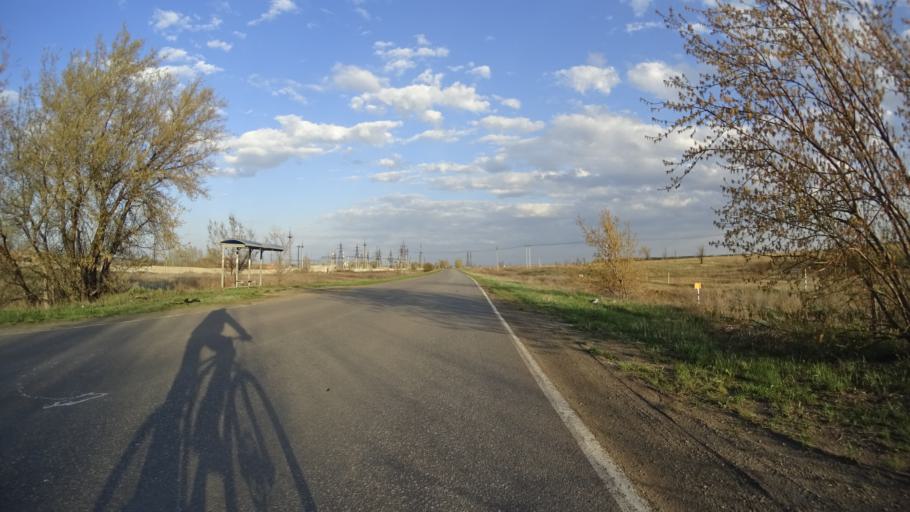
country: RU
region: Chelyabinsk
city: Troitsk
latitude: 54.0602
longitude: 61.5785
